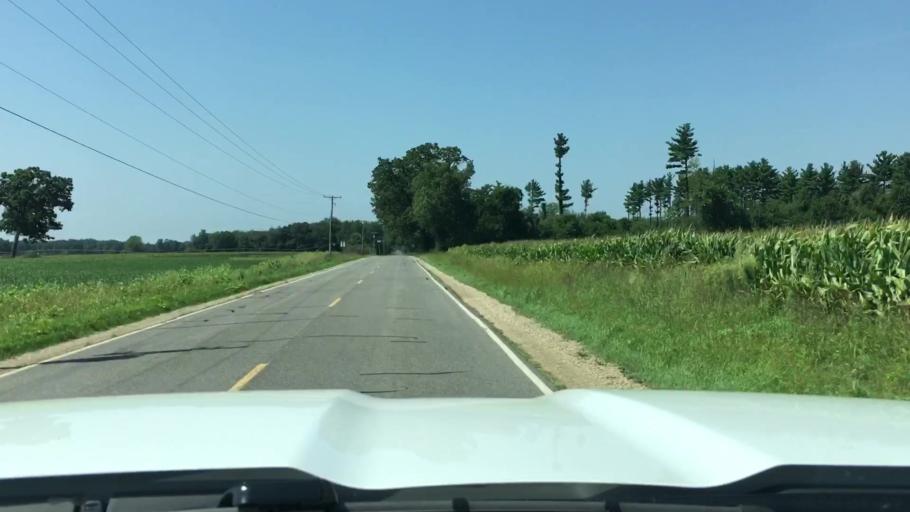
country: US
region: Michigan
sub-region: Saint Joseph County
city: Three Rivers
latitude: 41.9985
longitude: -85.5943
